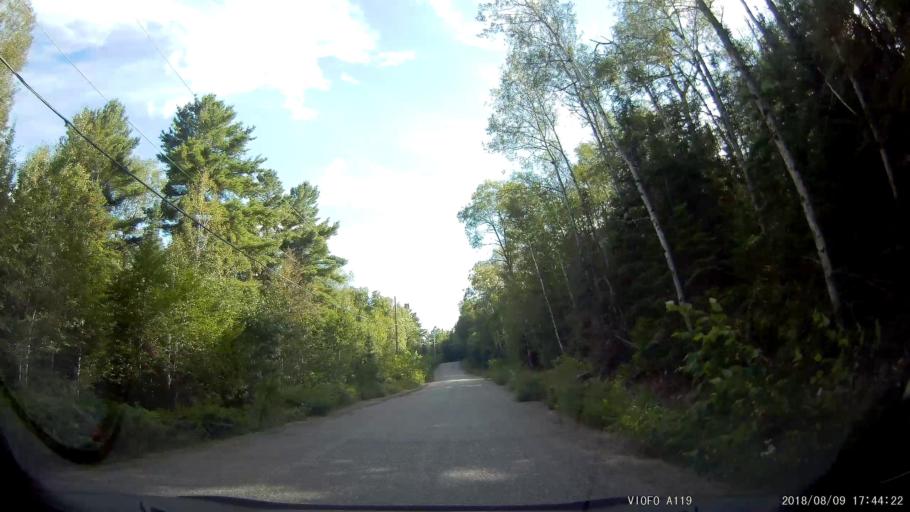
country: CA
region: Ontario
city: Rayside-Balfour
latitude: 46.6064
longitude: -81.5330
